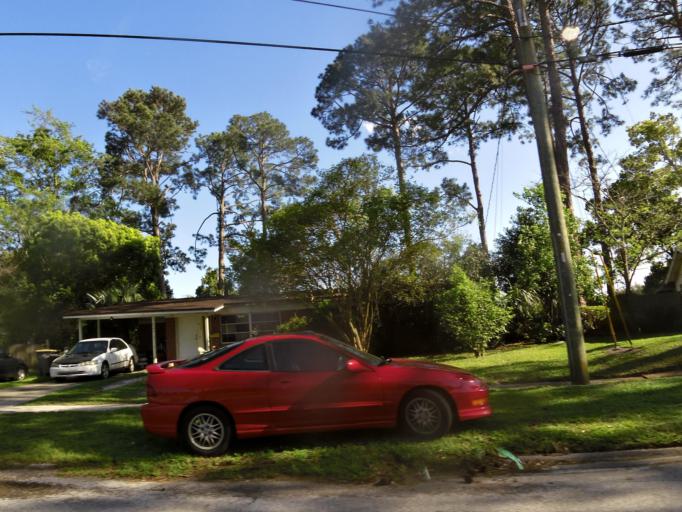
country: US
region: Florida
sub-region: Duval County
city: Jacksonville
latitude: 30.2741
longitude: -81.5971
